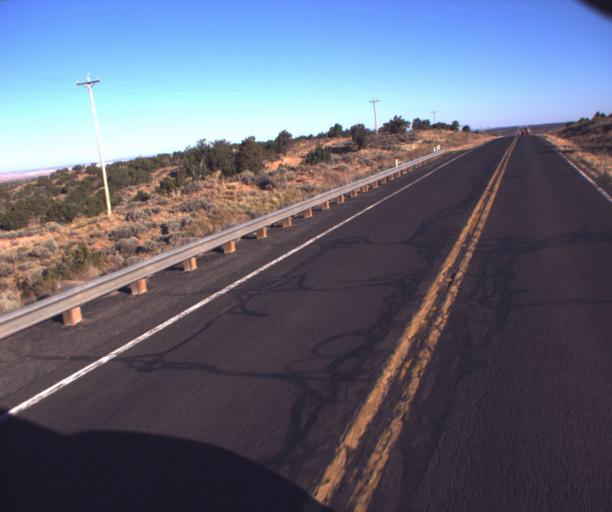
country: US
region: Arizona
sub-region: Apache County
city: Ganado
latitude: 35.5823
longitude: -109.5365
